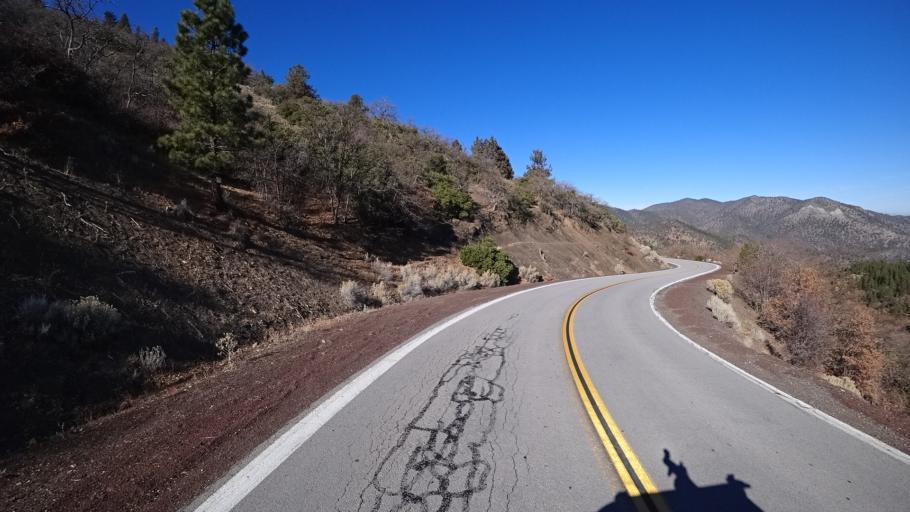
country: US
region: California
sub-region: Siskiyou County
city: Weed
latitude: 41.4398
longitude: -122.6418
